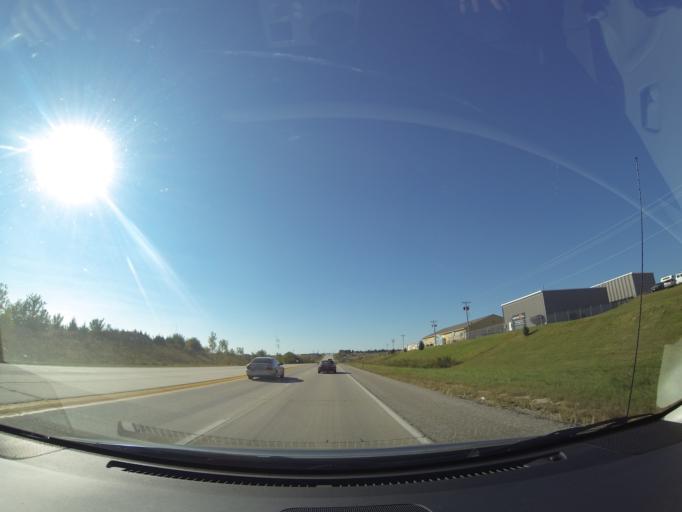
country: US
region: Nebraska
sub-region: Sarpy County
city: Gretna
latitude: 41.1089
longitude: -96.2535
